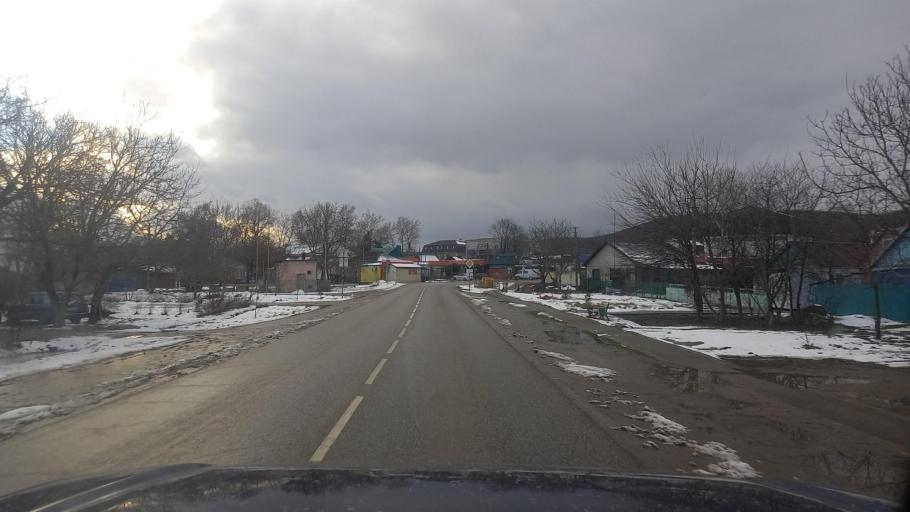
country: RU
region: Krasnodarskiy
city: Smolenskaya
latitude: 44.7860
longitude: 38.8004
